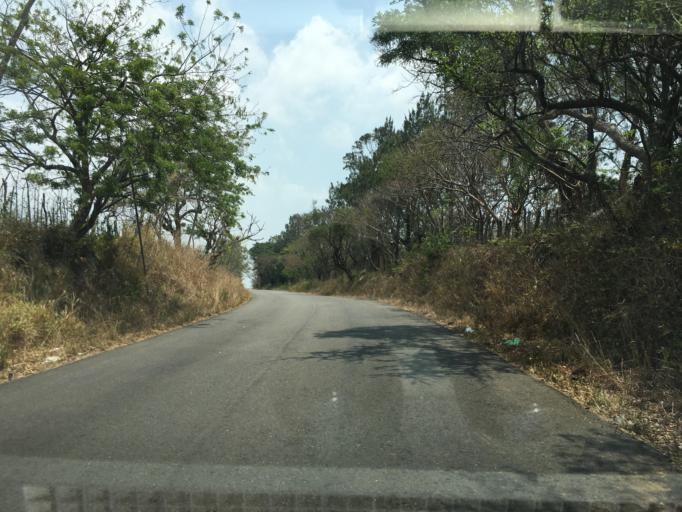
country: GT
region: Santa Rosa
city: Pueblo Nuevo Vinas
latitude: 14.3162
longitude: -90.5392
